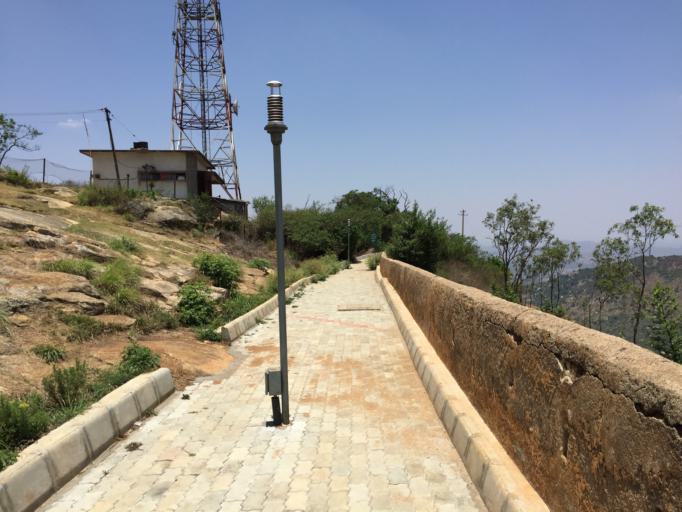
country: IN
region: Karnataka
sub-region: Chikkaballapur
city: Chik Ballapur
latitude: 13.3720
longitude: 77.6848
